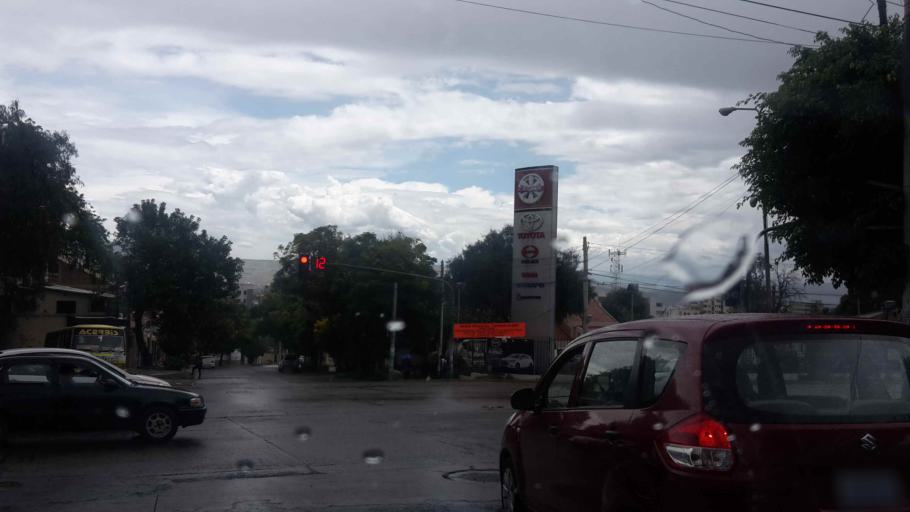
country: BO
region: Cochabamba
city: Cochabamba
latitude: -17.3646
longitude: -66.1620
